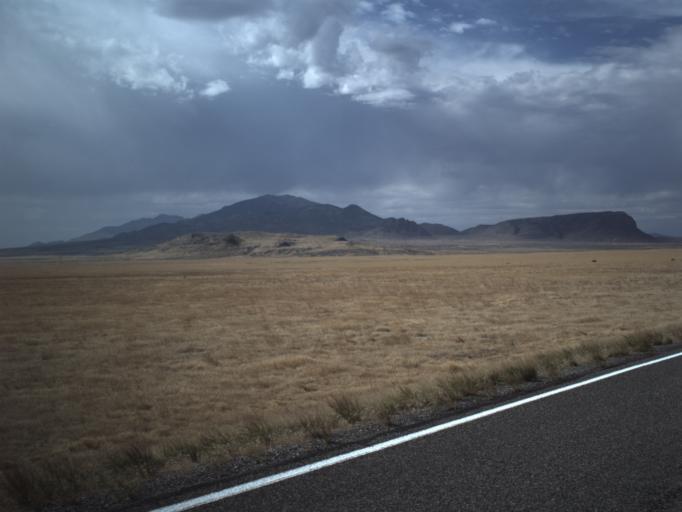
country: US
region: Utah
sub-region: Tooele County
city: Wendover
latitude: 41.3975
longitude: -113.9578
